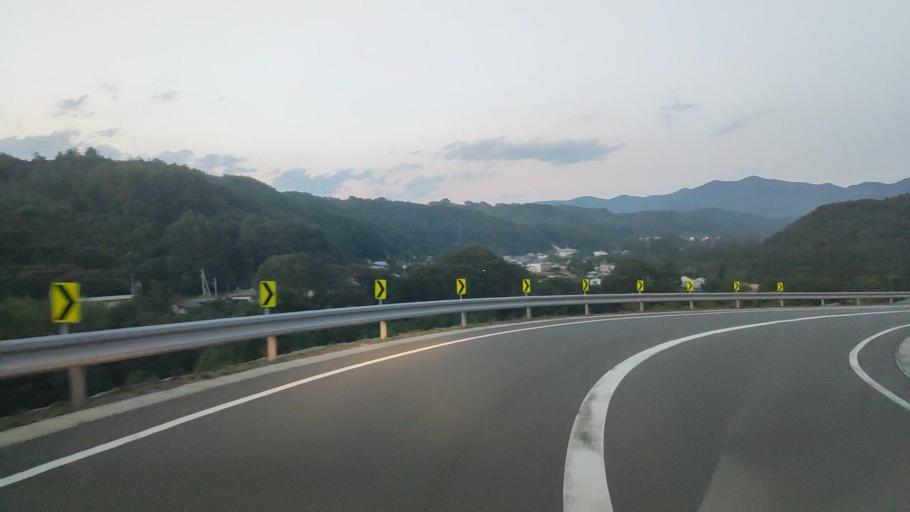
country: JP
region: Gunma
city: Nakanojomachi
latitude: 36.5456
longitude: 138.6003
